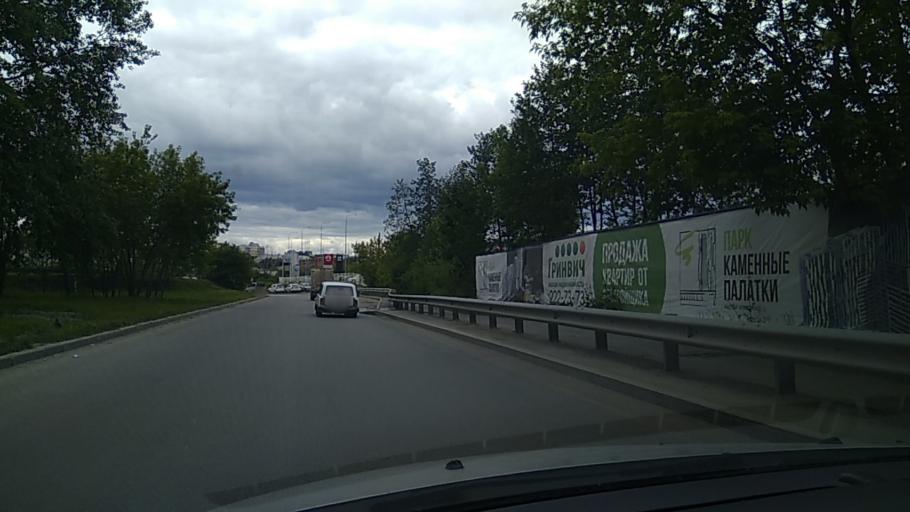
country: RU
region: Sverdlovsk
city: Yekaterinburg
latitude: 56.8422
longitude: 60.6734
